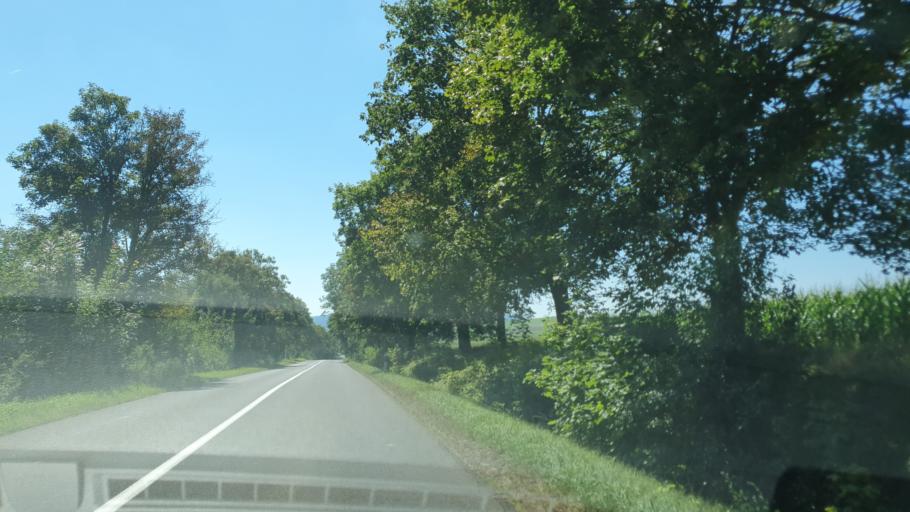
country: HU
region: Nograd
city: Rimoc
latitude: 48.0555
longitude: 19.5564
